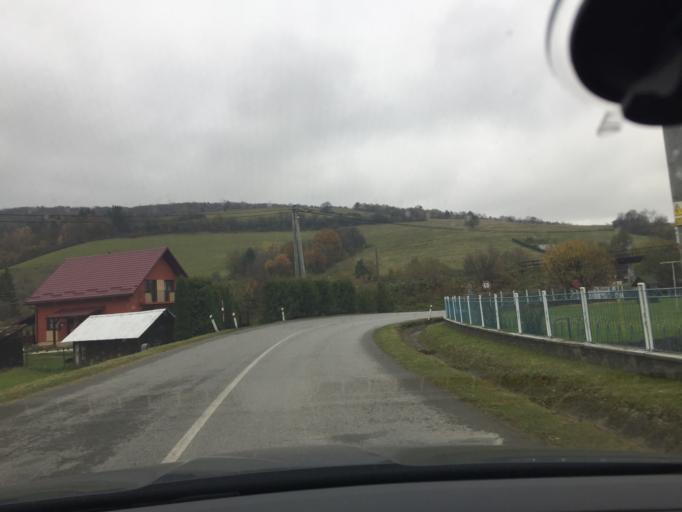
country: SK
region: Presovsky
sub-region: Okres Bardejov
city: Bardejov
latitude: 49.2570
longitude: 21.2467
